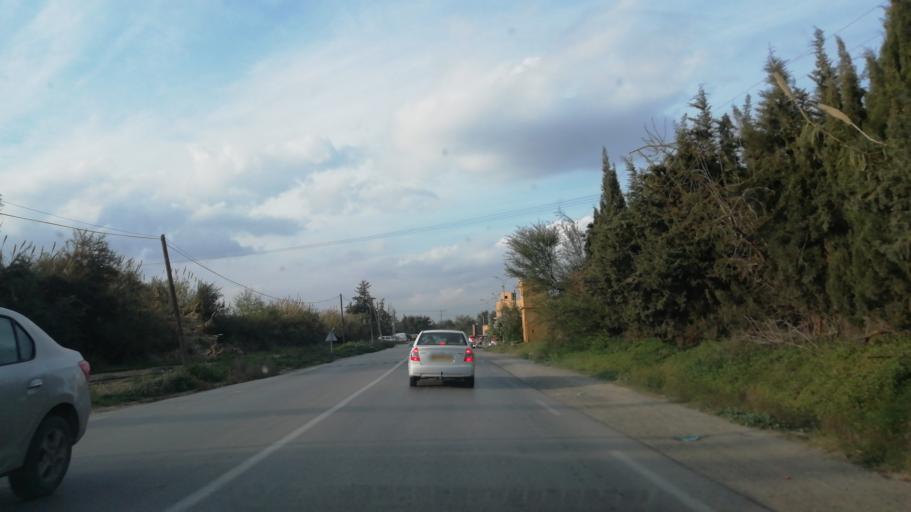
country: DZ
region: Mascara
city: Mascara
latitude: 35.5984
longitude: 0.0540
